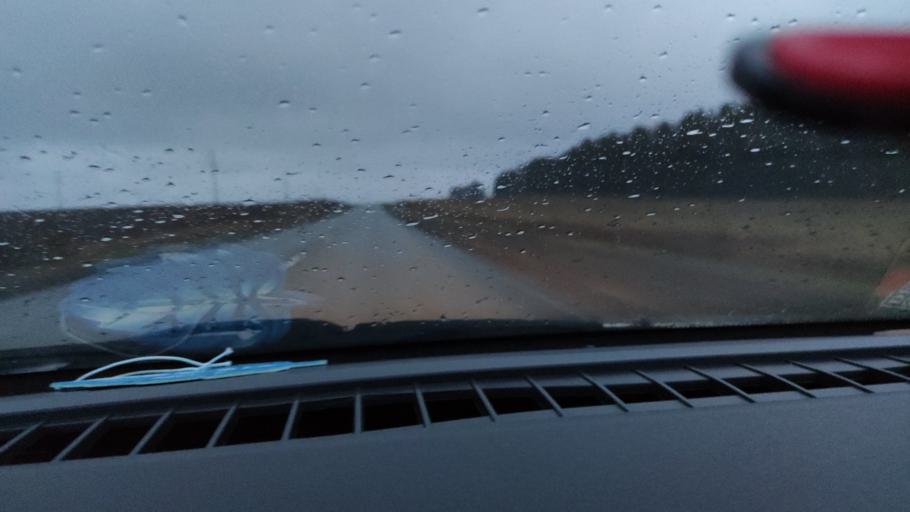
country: RU
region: Udmurtiya
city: Alnashi
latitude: 56.2892
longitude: 52.3536
